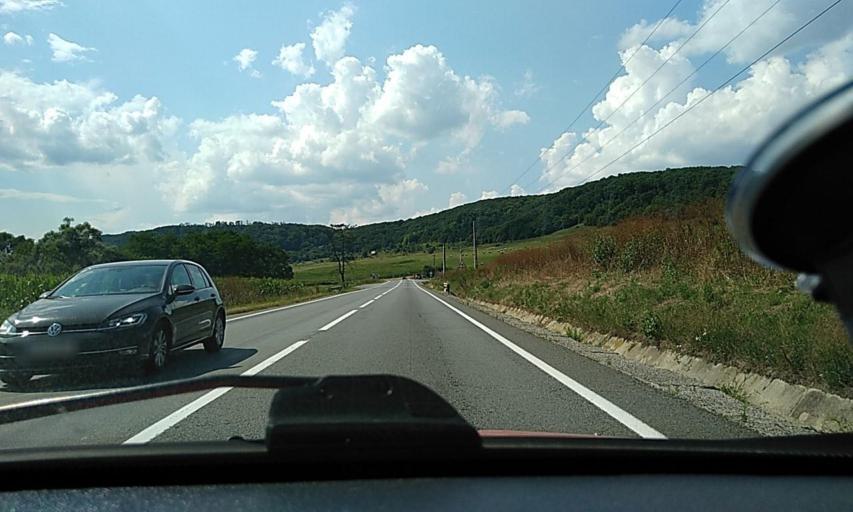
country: RO
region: Brasov
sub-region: Comuna Bunesti
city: Bunesti
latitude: 46.0990
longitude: 25.0932
